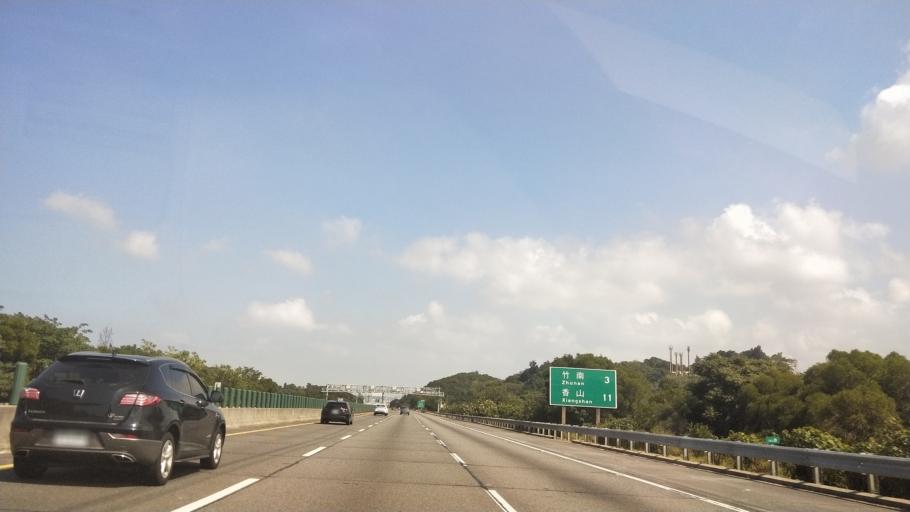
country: TW
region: Taiwan
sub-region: Miaoli
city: Miaoli
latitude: 24.6543
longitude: 120.8366
